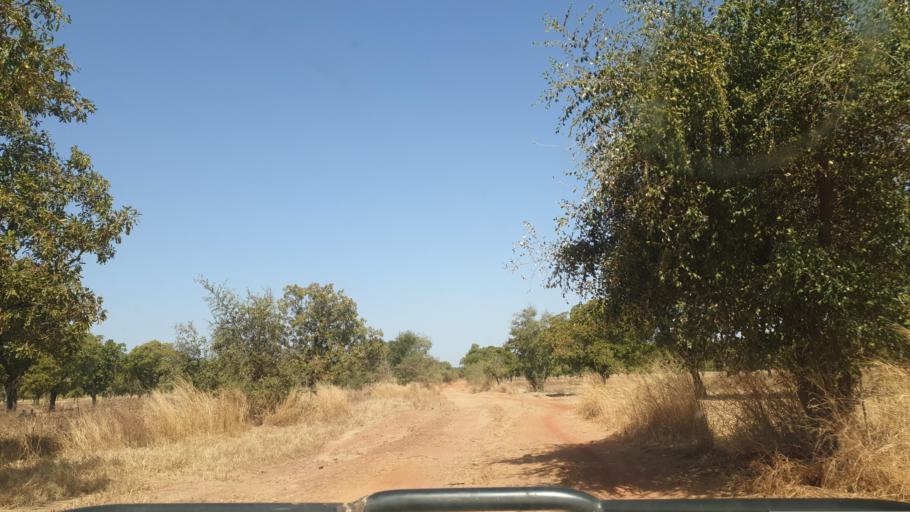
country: ML
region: Koulikoro
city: Dioila
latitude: 11.9019
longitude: -6.9820
